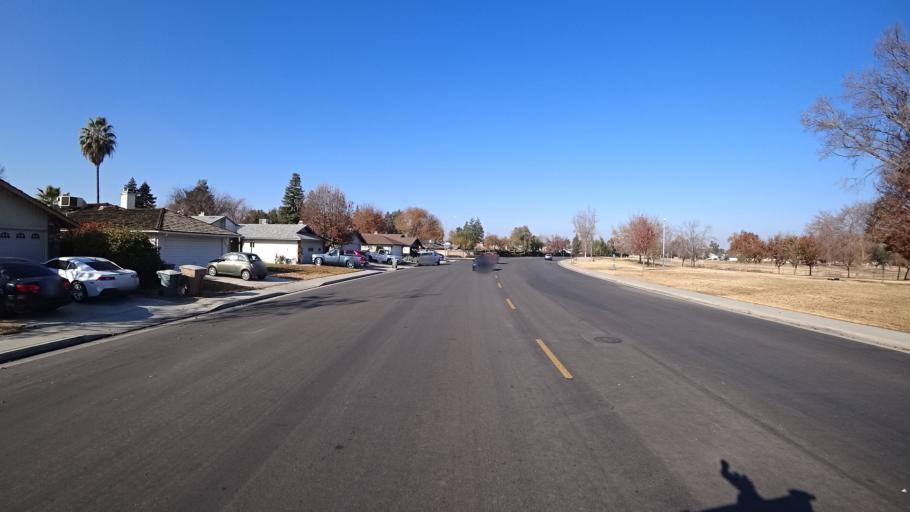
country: US
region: California
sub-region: Kern County
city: Greenacres
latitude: 35.3203
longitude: -119.1063
